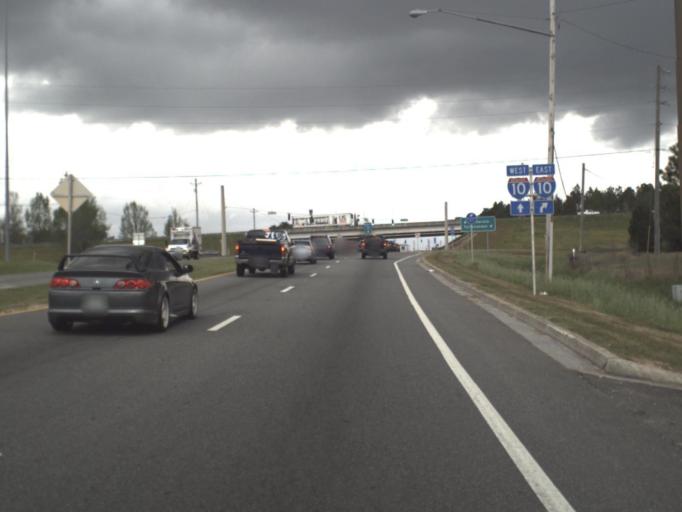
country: US
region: Florida
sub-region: Okaloosa County
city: Crestview
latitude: 30.7233
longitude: -86.5689
